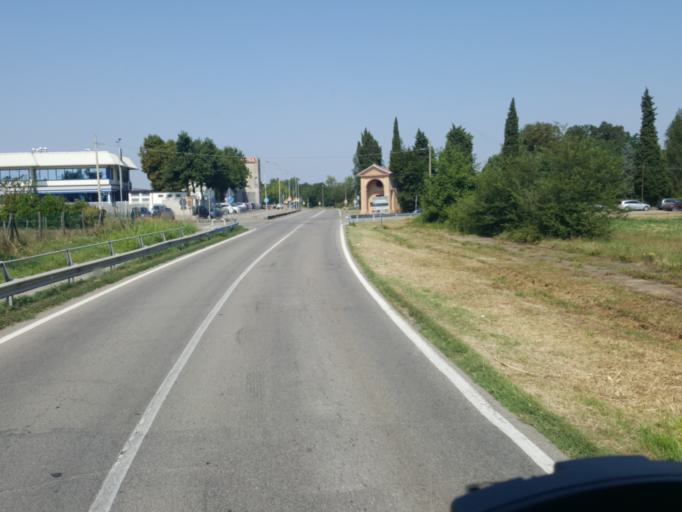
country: IT
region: Emilia-Romagna
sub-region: Provincia di Modena
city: Ca' di Sola
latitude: 44.5387
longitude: 10.9703
